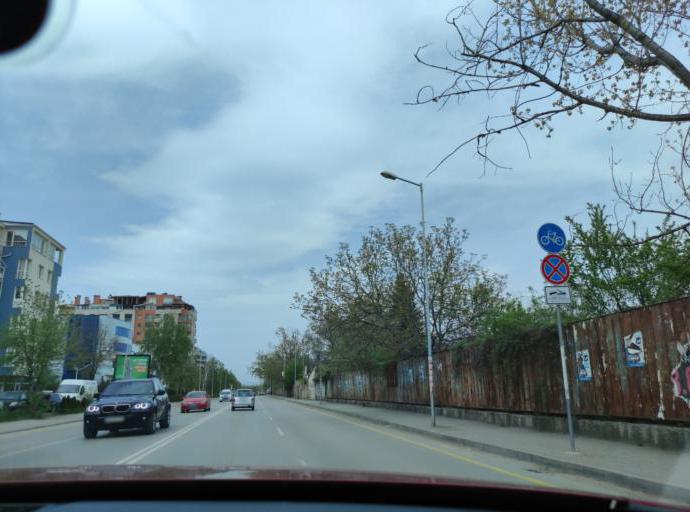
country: BG
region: Sofia-Capital
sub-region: Stolichna Obshtina
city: Sofia
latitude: 42.6472
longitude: 23.3455
